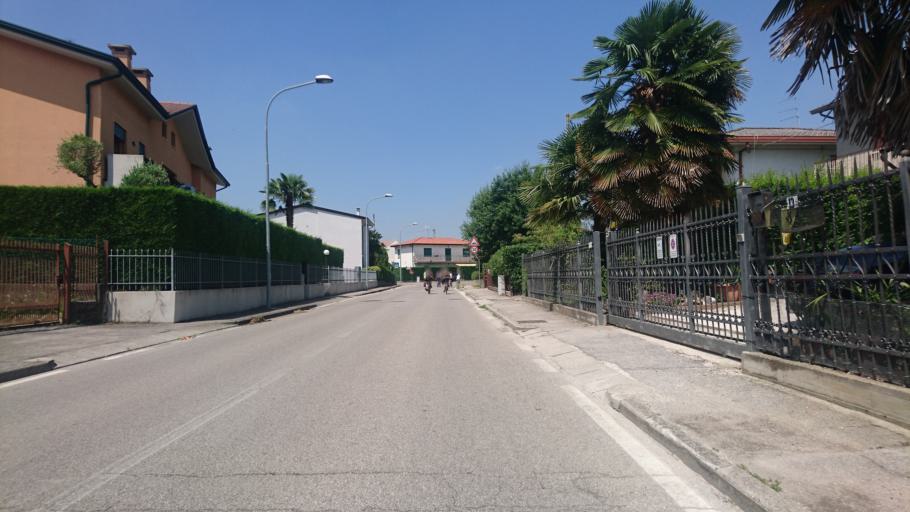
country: IT
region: Veneto
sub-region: Provincia di Venezia
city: Galta
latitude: 45.3908
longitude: 12.0237
